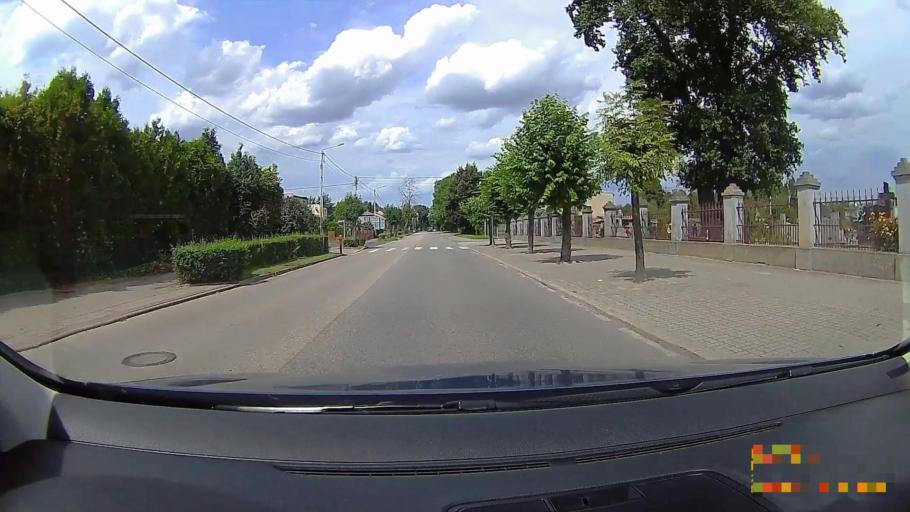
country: PL
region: Greater Poland Voivodeship
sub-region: Powiat koninski
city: Rychwal
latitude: 52.0750
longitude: 18.1625
